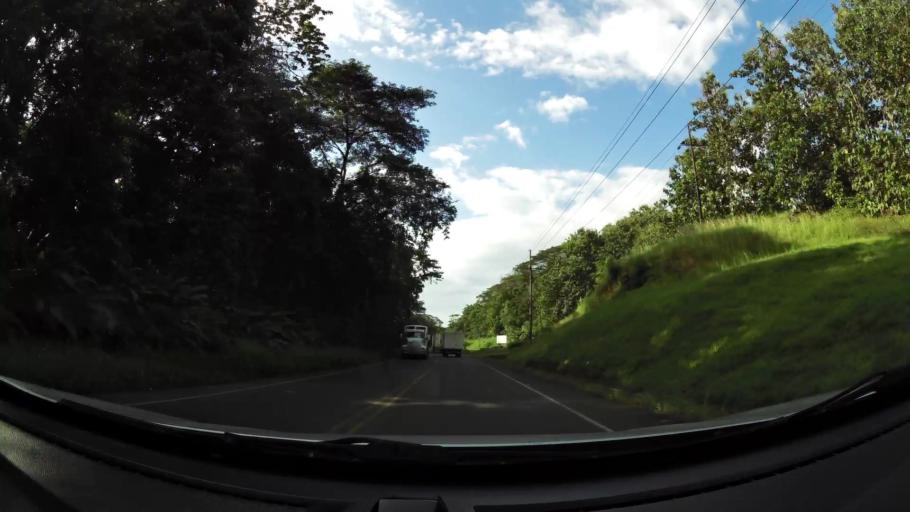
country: CR
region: Puntarenas
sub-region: Canton de Garabito
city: Jaco
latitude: 9.7335
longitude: -84.6286
